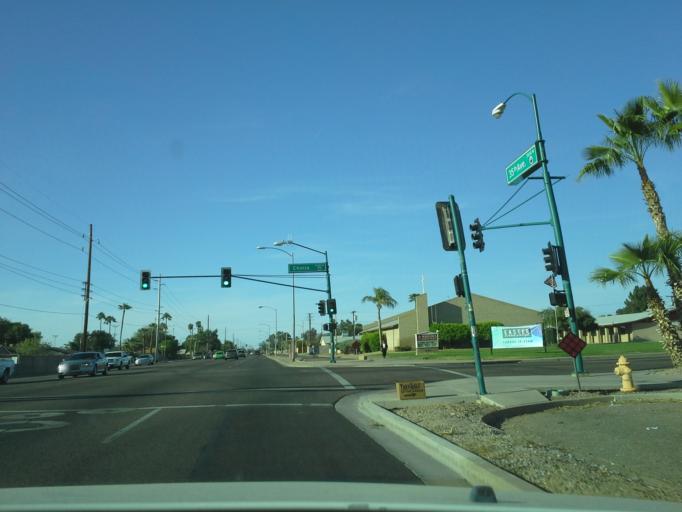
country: US
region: Arizona
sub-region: Maricopa County
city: Glendale
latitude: 33.5888
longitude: -112.1340
